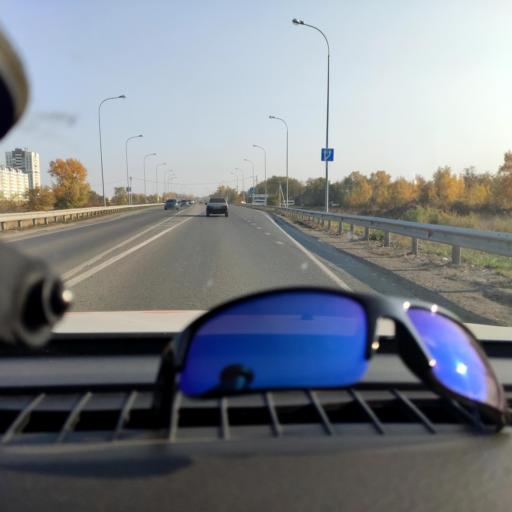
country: RU
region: Samara
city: Samara
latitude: 53.1089
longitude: 50.1320
